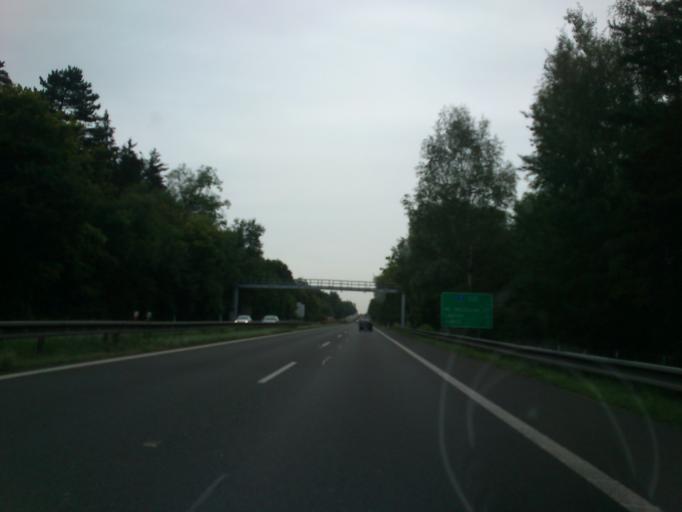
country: CZ
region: Central Bohemia
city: Celakovice
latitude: 50.2277
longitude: 14.7234
